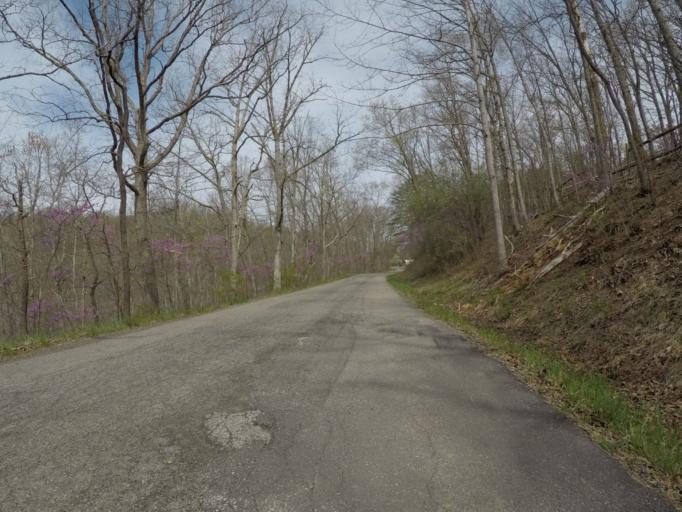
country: US
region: West Virginia
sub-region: Wayne County
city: Lavalette
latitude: 38.3506
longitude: -82.3987
